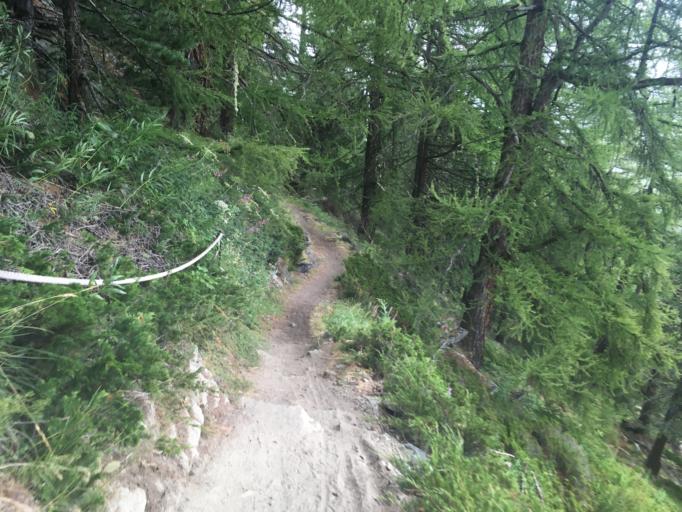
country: CH
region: Valais
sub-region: Visp District
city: Zermatt
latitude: 46.0079
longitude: 7.7266
